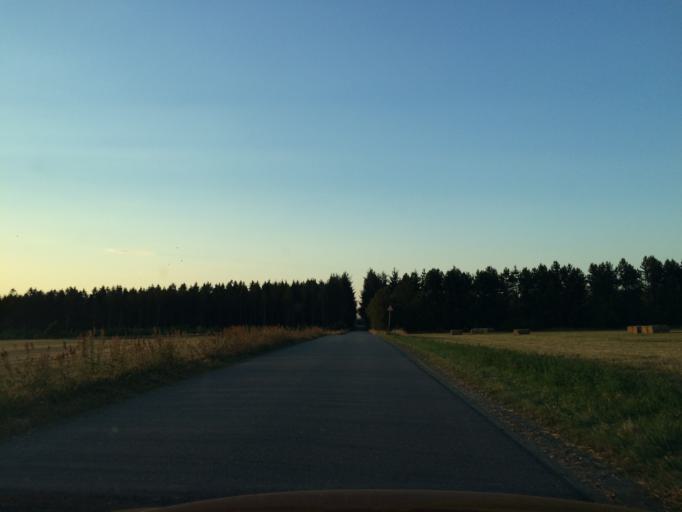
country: DK
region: Central Jutland
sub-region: Silkeborg Kommune
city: Svejbaek
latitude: 56.2238
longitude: 9.6822
